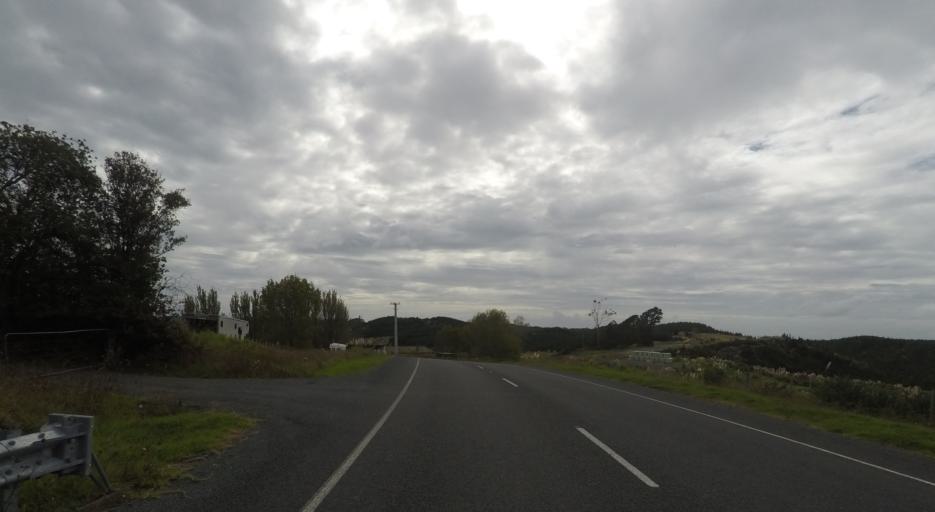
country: NZ
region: Auckland
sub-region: Auckland
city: Rothesay Bay
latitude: -36.6548
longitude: 174.6887
